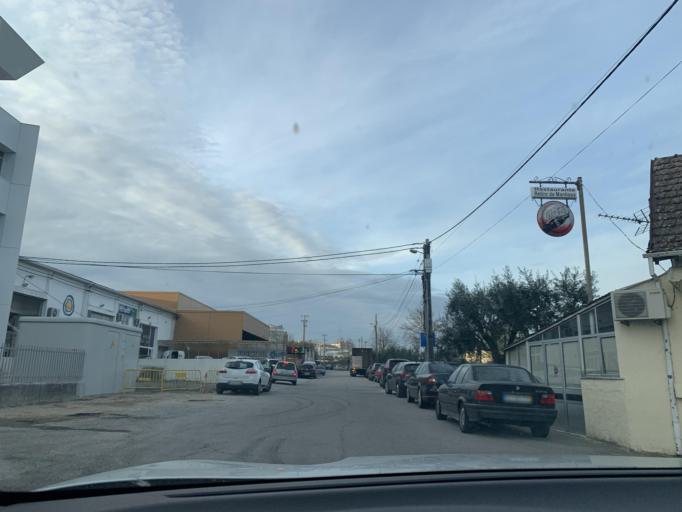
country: PT
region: Viseu
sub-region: Viseu
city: Viseu
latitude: 40.6414
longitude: -7.9087
